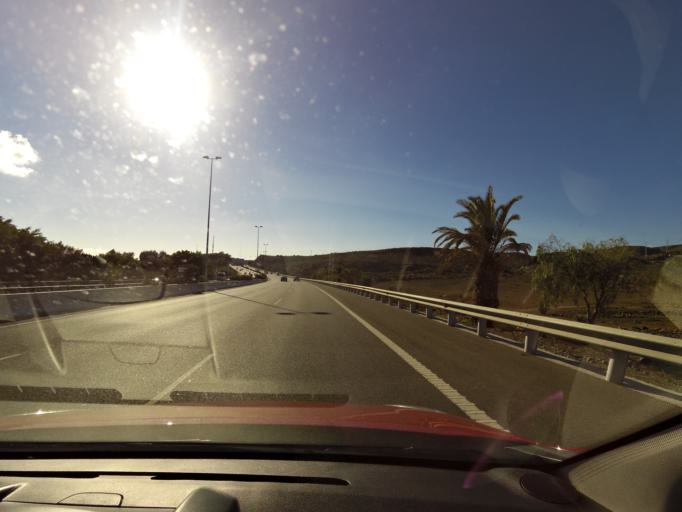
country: ES
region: Canary Islands
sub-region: Provincia de Las Palmas
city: Playa del Ingles
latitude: 27.7869
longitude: -15.5196
